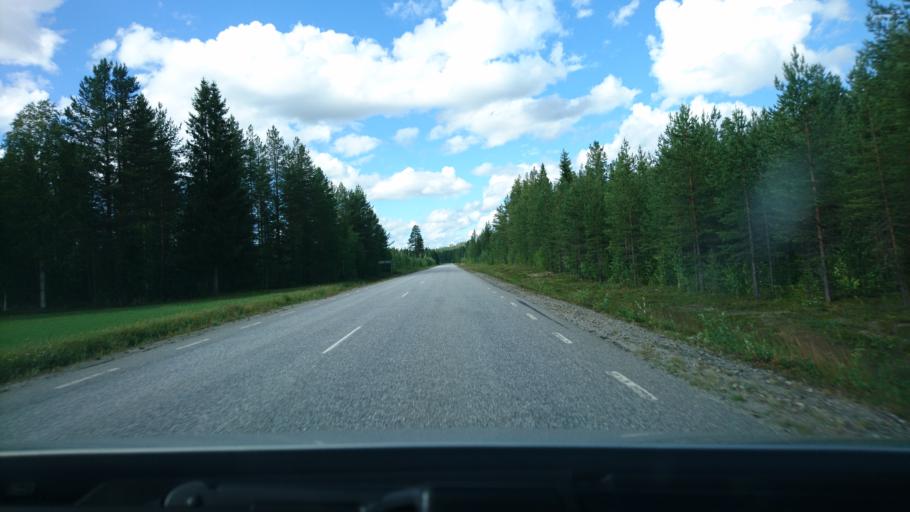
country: SE
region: Vaesterbotten
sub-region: Asele Kommun
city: Asele
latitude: 64.0369
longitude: 17.2947
